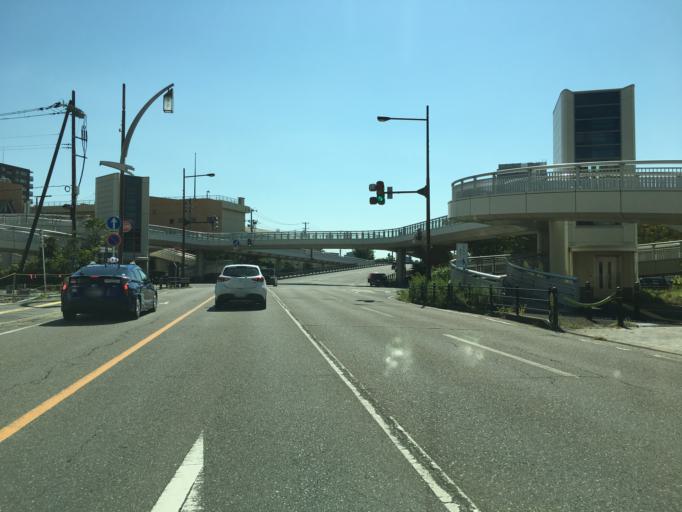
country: JP
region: Niigata
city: Niigata-shi
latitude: 37.9147
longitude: 139.0410
